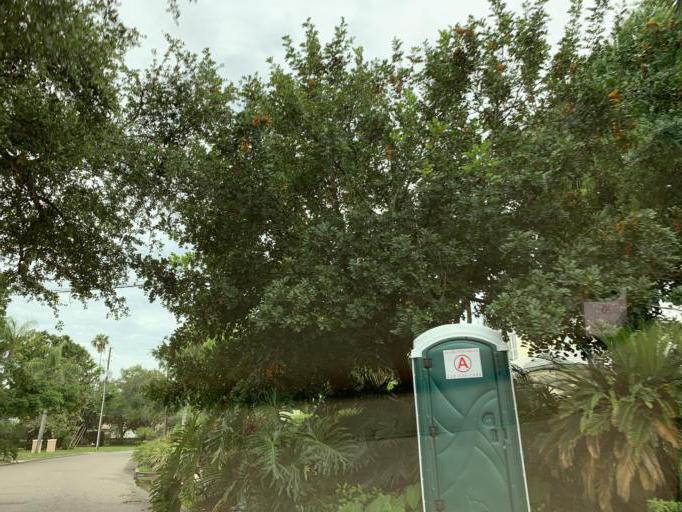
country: US
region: Florida
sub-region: Pinellas County
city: Gandy
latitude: 27.7970
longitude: -82.6068
